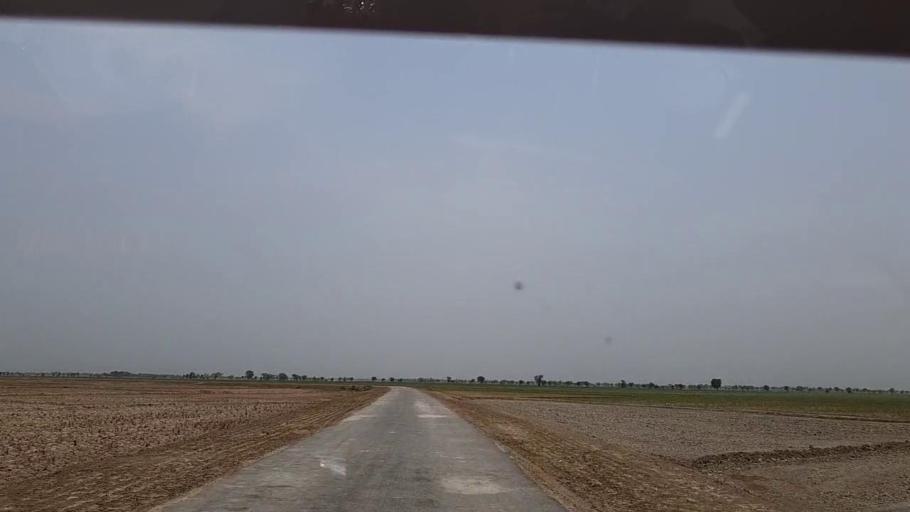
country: PK
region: Sindh
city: Khairpur Nathan Shah
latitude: 27.0194
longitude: 67.6444
